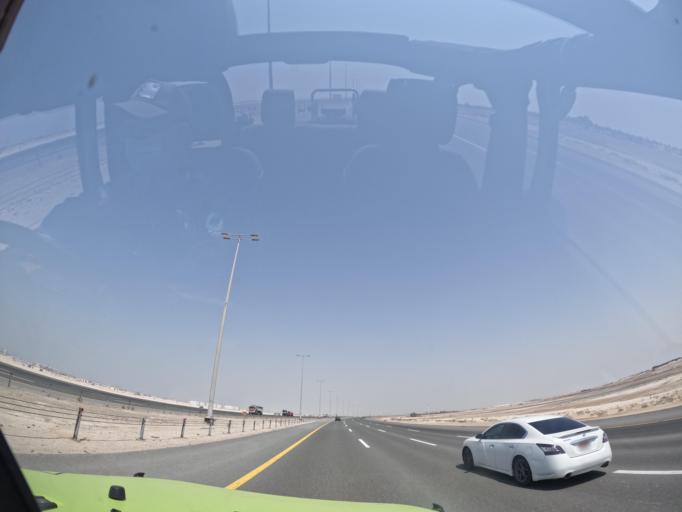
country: AE
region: Abu Dhabi
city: Abu Dhabi
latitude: 24.2658
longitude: 54.4942
